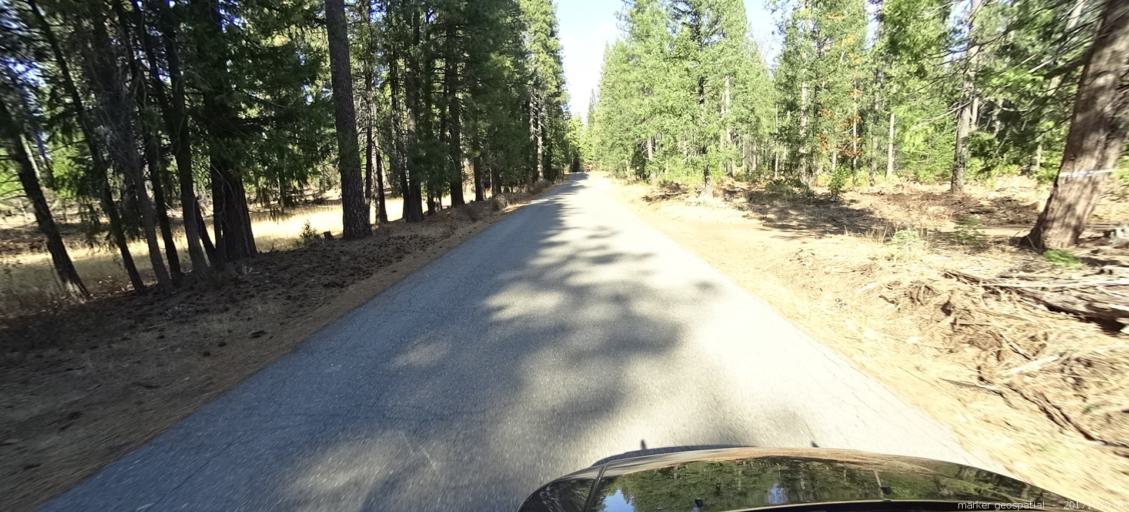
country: US
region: California
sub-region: Shasta County
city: Shingletown
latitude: 40.5158
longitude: -121.7242
